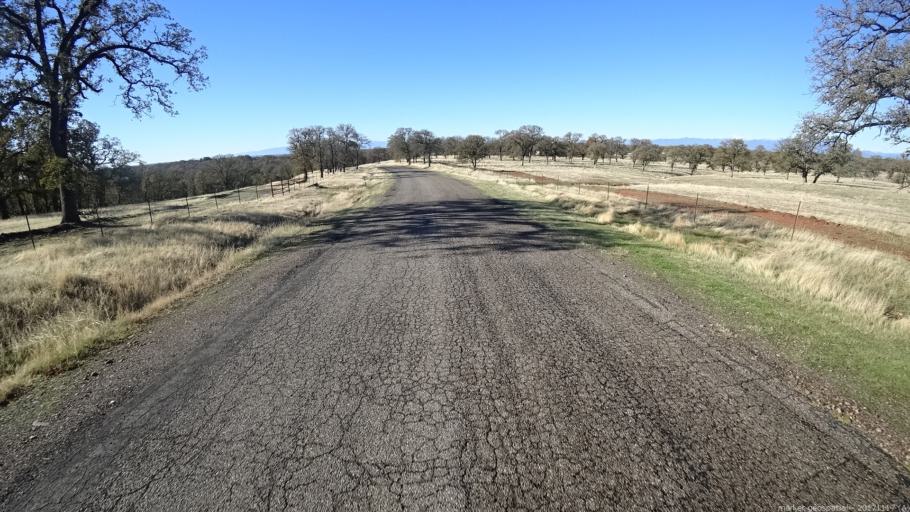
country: US
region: California
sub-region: Shasta County
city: Cottonwood
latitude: 40.4245
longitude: -122.1857
